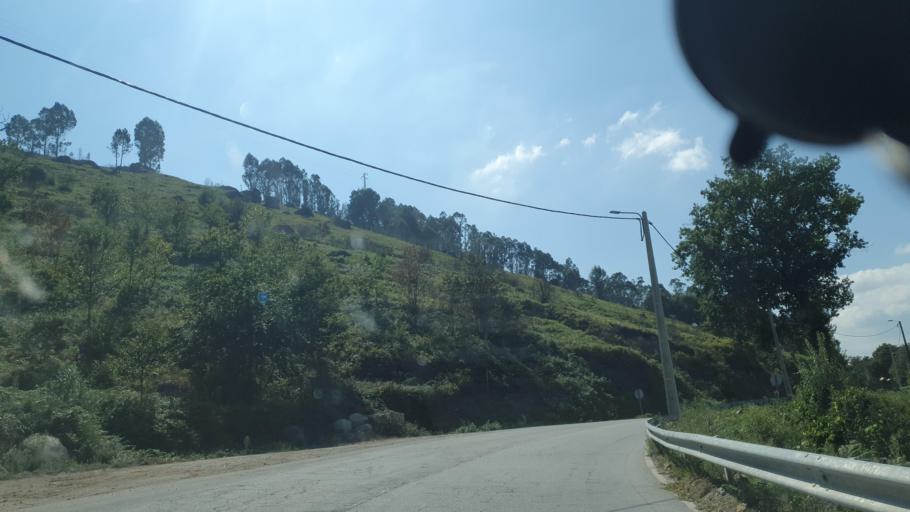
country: PT
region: Braga
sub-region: Vieira do Minho
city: Vieira do Minho
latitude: 41.6719
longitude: -8.1495
